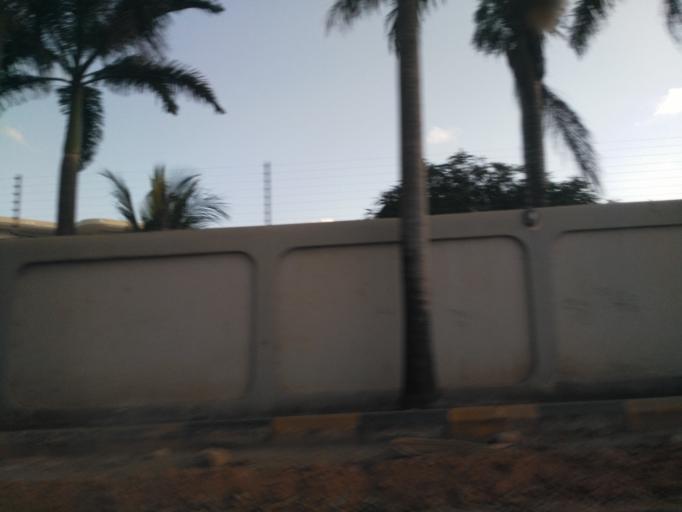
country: TZ
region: Dar es Salaam
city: Magomeni
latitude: -6.7610
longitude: 39.2644
